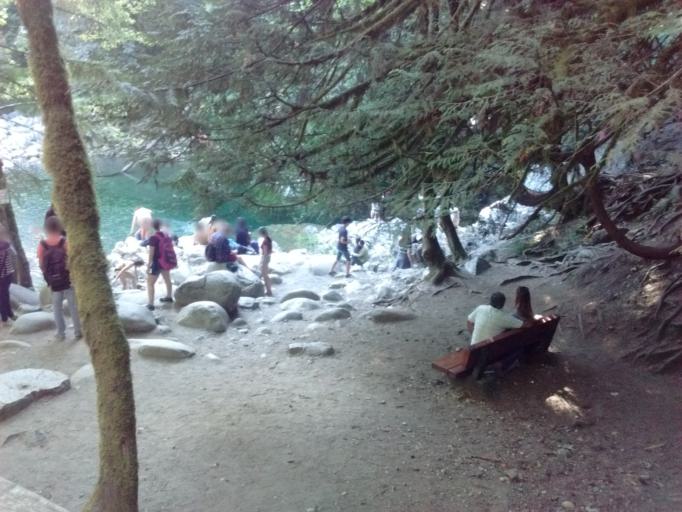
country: CA
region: British Columbia
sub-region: Fraser Valley Regional District
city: North Vancouver
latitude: 49.3473
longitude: -123.0202
